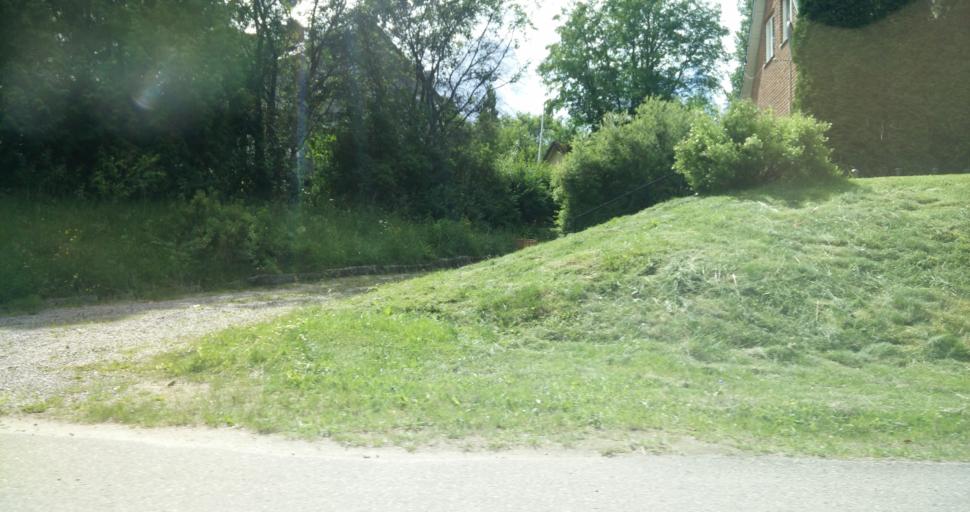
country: SE
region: Vaermland
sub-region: Hagfors Kommun
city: Hagfors
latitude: 60.0189
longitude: 13.6842
